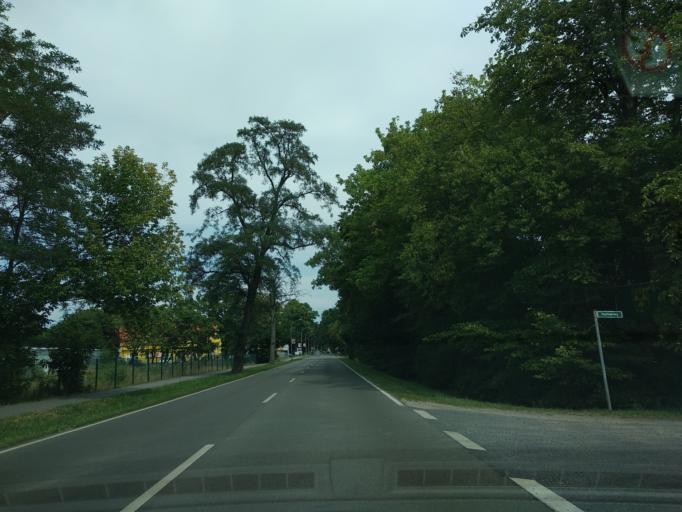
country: DE
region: Brandenburg
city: Leegebruch
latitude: 52.7508
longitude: 13.2000
